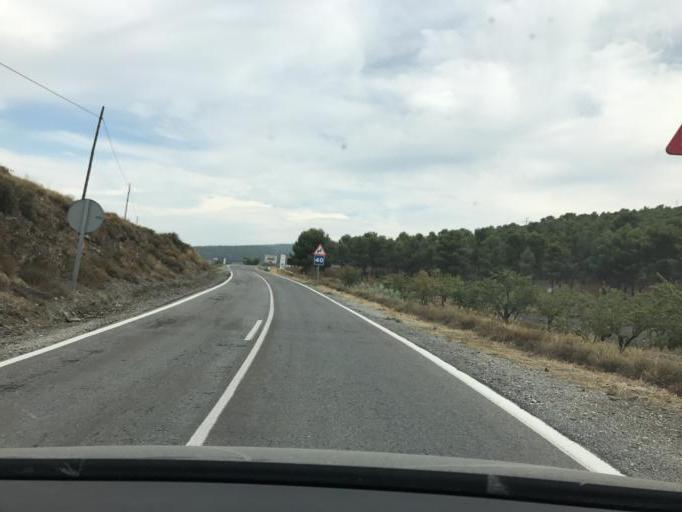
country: ES
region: Andalusia
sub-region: Provincia de Granada
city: Ferreira
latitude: 37.1755
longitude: -3.0490
